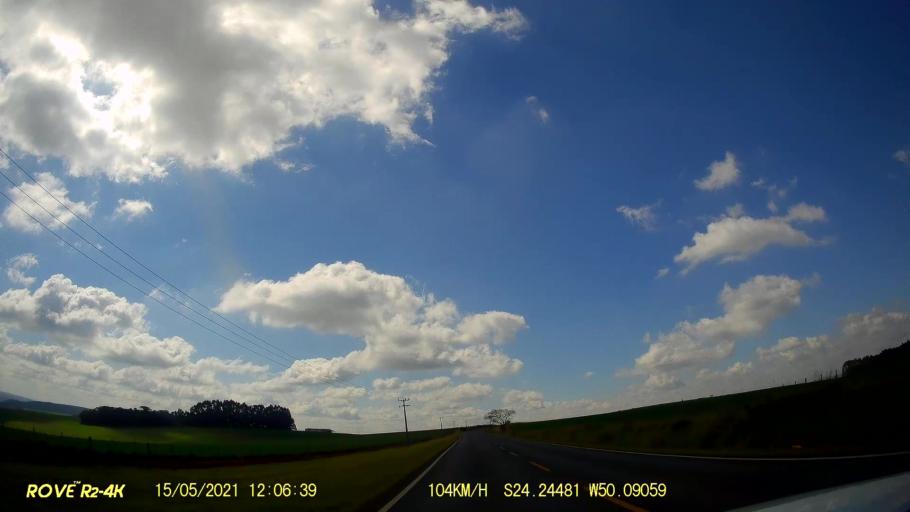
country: BR
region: Parana
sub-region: Pirai Do Sul
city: Pirai do Sul
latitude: -24.2448
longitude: -50.0906
